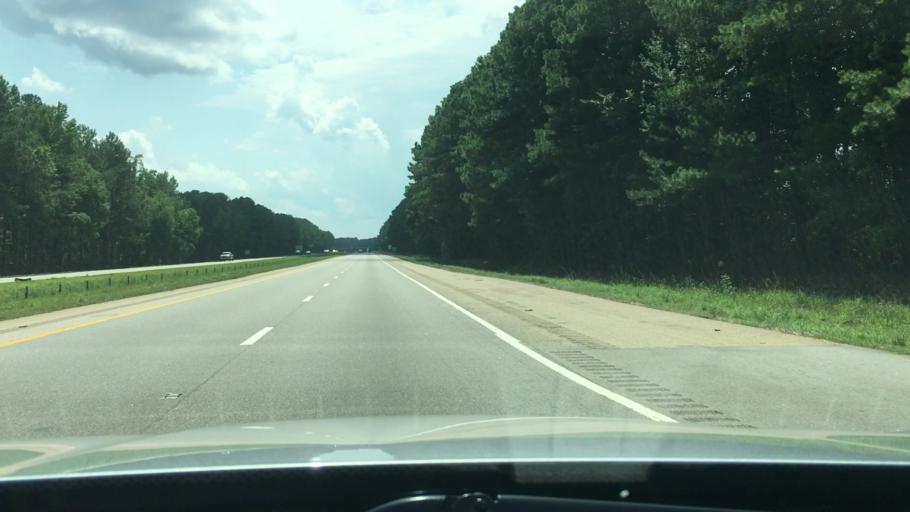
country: US
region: North Carolina
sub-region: Wilson County
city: Lucama
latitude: 35.7264
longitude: -78.0219
